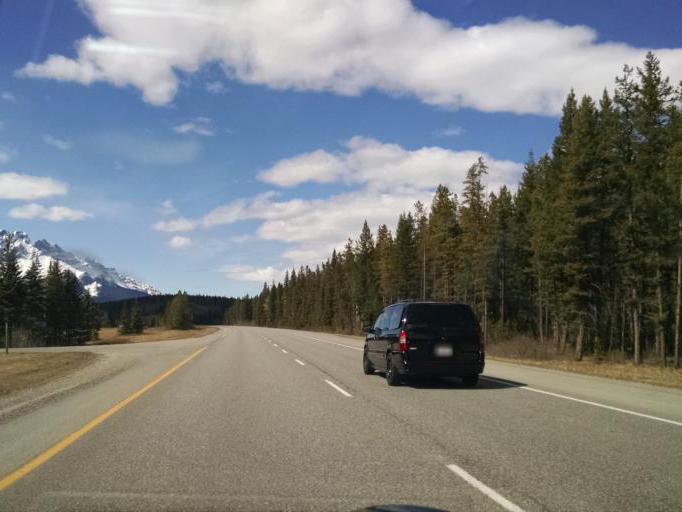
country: CA
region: Alberta
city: Canmore
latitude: 51.1541
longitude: -115.4331
